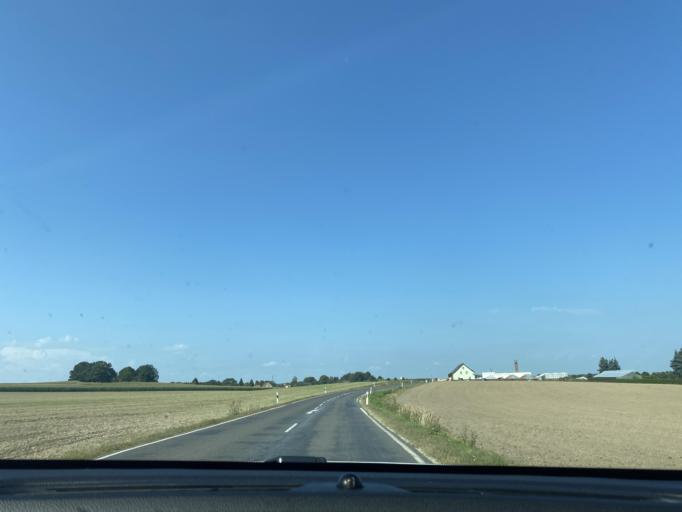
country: DE
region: Saxony
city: Reichenbach
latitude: 51.1829
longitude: 14.7665
